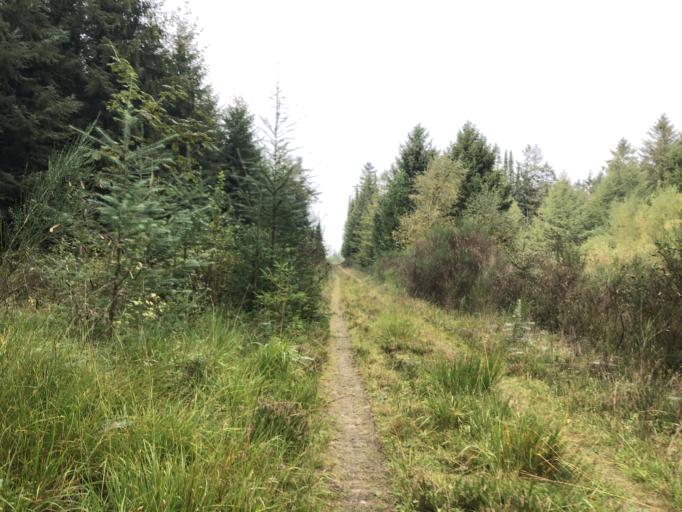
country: DK
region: Central Jutland
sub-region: Holstebro Kommune
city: Ulfborg
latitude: 56.2491
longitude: 8.4606
